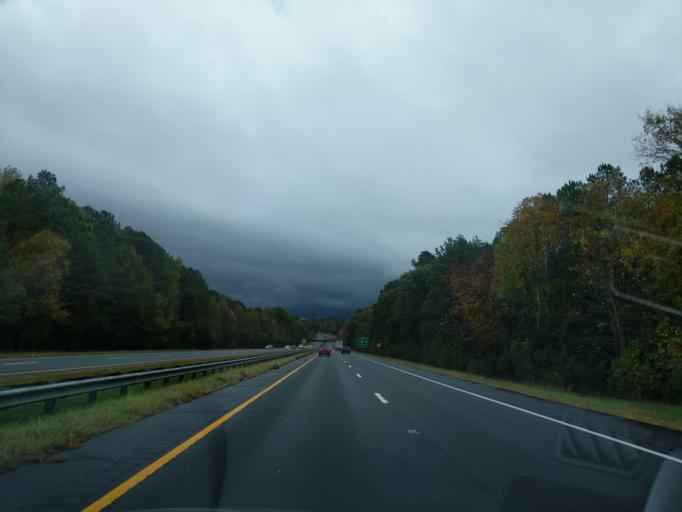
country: US
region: North Carolina
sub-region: Orange County
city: Hillsborough
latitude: 36.0432
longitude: -79.0366
